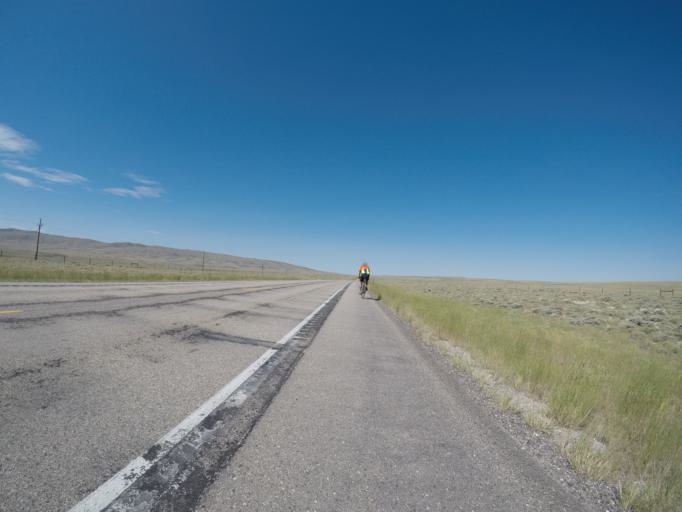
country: US
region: Wyoming
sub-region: Carbon County
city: Saratoga
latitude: 41.8072
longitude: -106.6907
